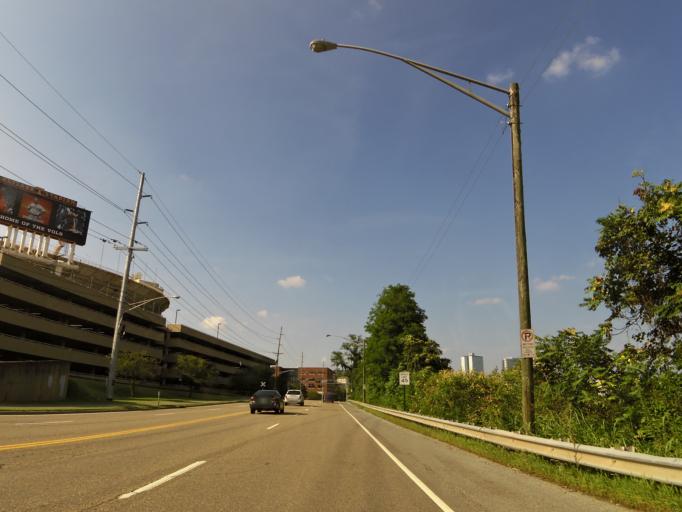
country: US
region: Tennessee
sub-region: Knox County
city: Knoxville
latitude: 35.9525
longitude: -83.9235
